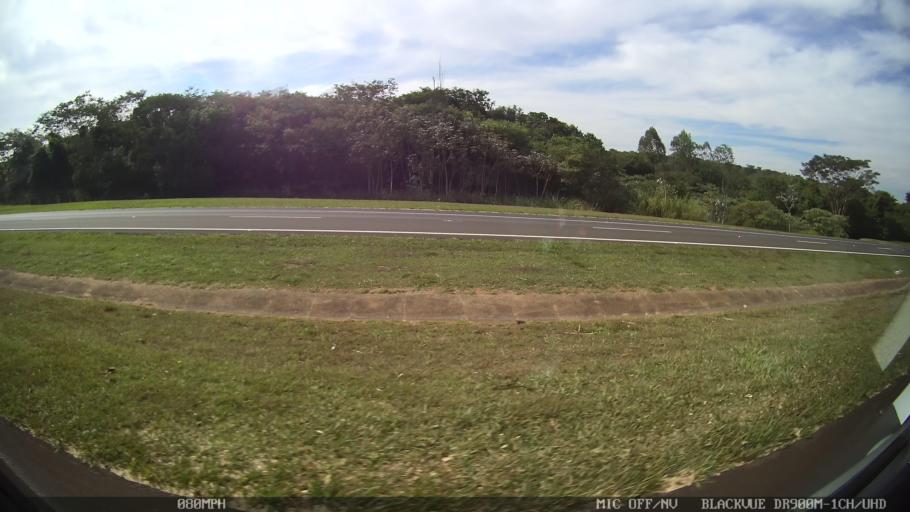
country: BR
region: Sao Paulo
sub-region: Matao
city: Matao
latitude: -21.6137
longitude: -48.4204
